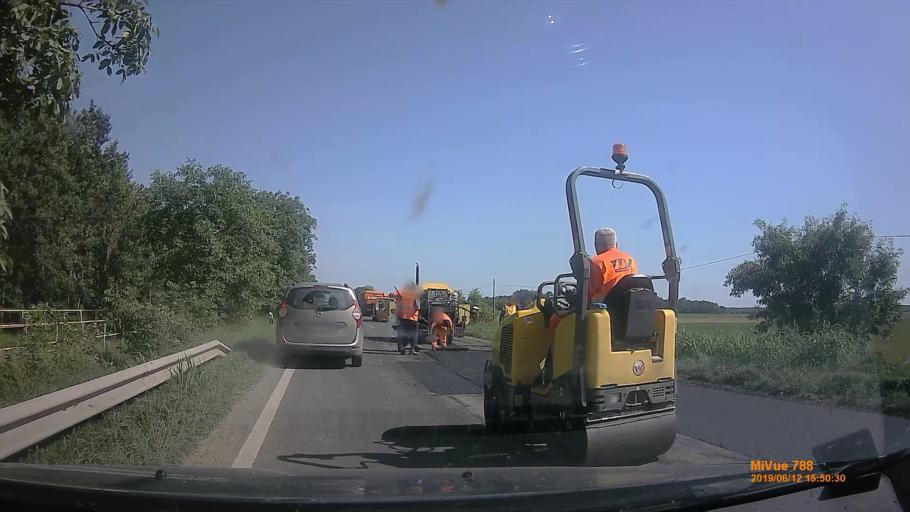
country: HU
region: Csongrad
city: Apatfalva
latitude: 46.1865
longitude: 20.5661
